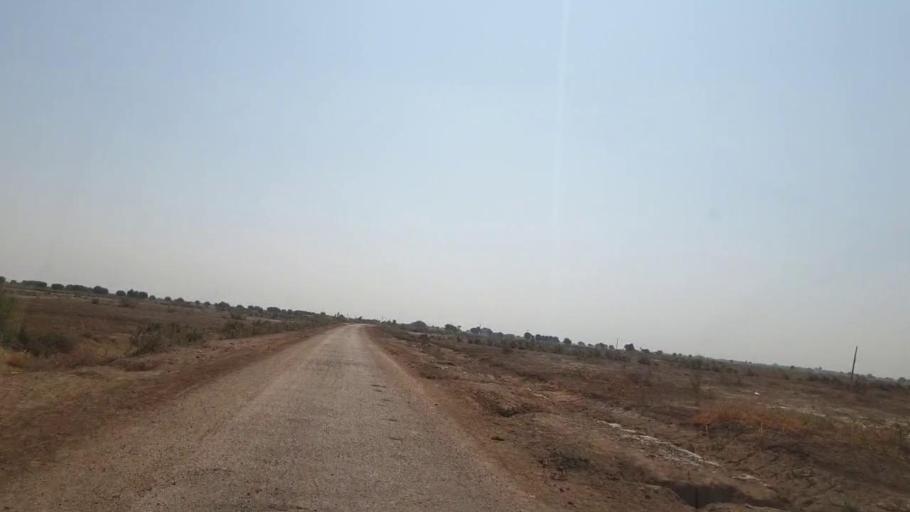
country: PK
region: Sindh
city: Kunri
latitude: 25.0862
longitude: 69.4735
